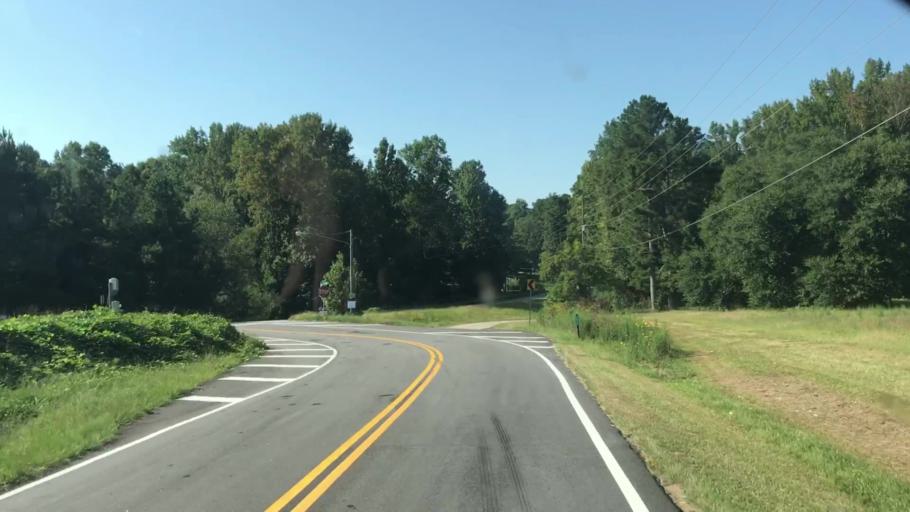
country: US
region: Georgia
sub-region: Walton County
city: Loganville
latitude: 33.8976
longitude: -83.8045
